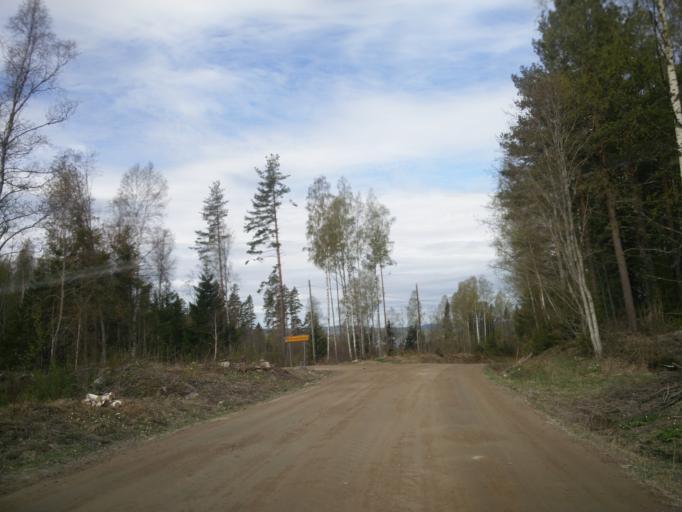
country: SE
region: Vaesternorrland
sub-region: Sundsvalls Kommun
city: Vi
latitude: 62.2701
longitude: 17.1802
